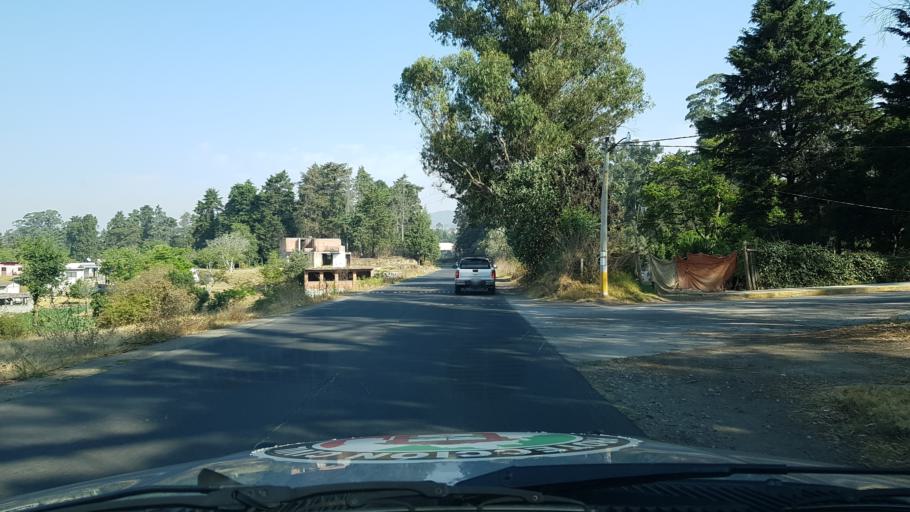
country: MX
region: Mexico
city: Ozumba de Alzate
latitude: 19.0522
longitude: -98.7844
